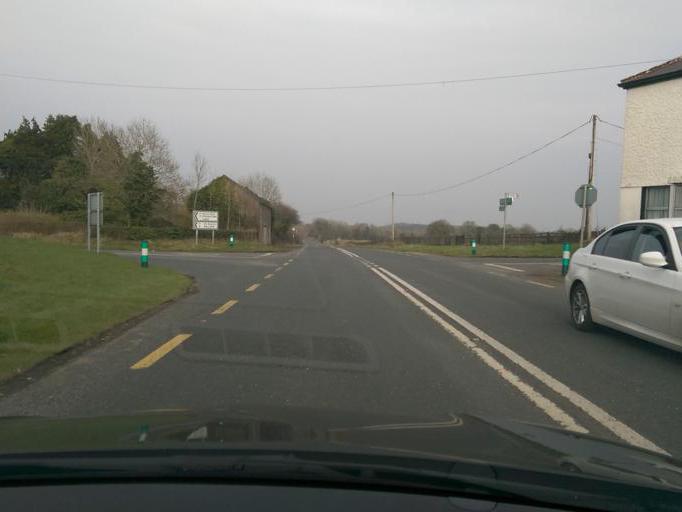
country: IE
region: Connaught
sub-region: Roscommon
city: Roscommon
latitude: 53.6527
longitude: -8.1098
